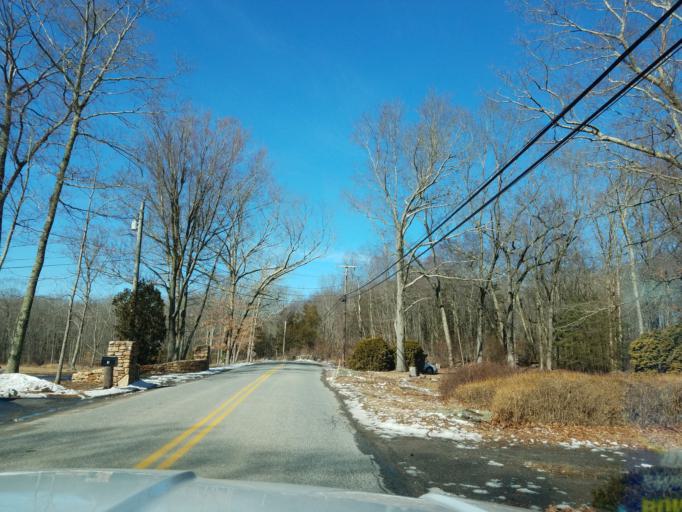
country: US
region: Connecticut
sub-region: New London County
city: Old Mystic
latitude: 41.4473
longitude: -71.9110
